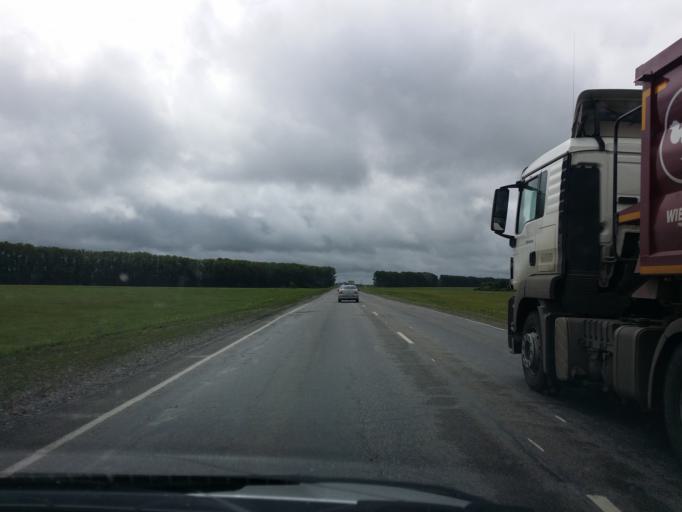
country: RU
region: Altai Krai
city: Zonal'noye
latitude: 52.8095
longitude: 84.8844
